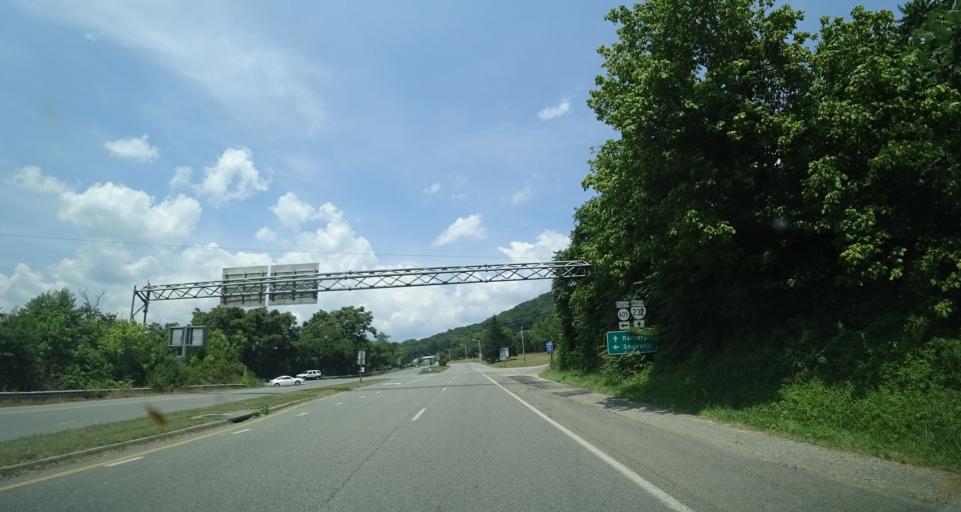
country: US
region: Virginia
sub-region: City of Radford
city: Radford
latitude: 37.0930
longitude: -80.5779
